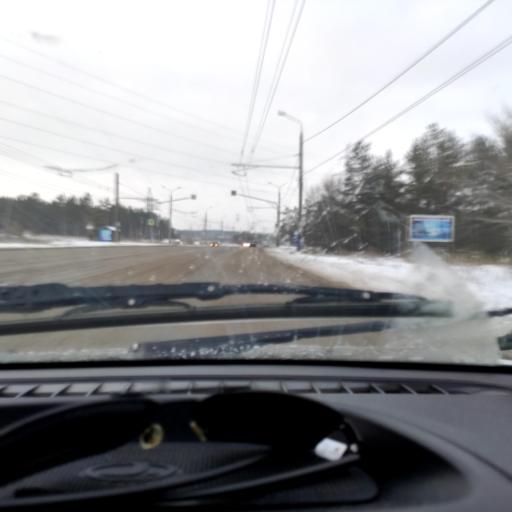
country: RU
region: Samara
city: Zhigulevsk
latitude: 53.4964
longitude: 49.5072
